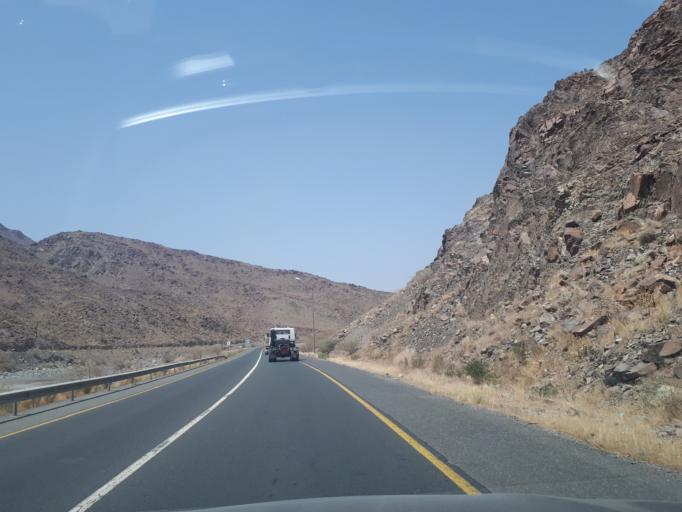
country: OM
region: Muhafazat ad Dakhiliyah
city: Sufalat Sama'il
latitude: 23.2511
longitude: 58.0984
